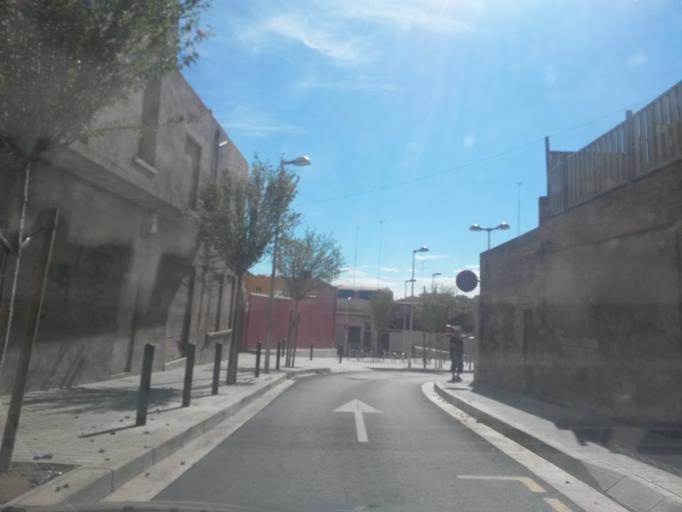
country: ES
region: Catalonia
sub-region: Provincia de Barcelona
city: Llefia
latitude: 41.4468
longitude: 2.2308
